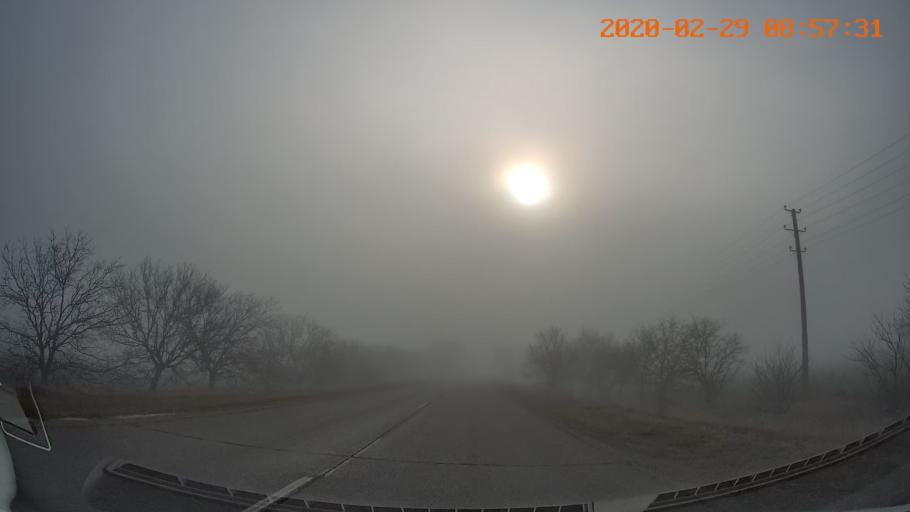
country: MD
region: Telenesti
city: Tiraspolul Nou
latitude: 46.9276
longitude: 29.6275
